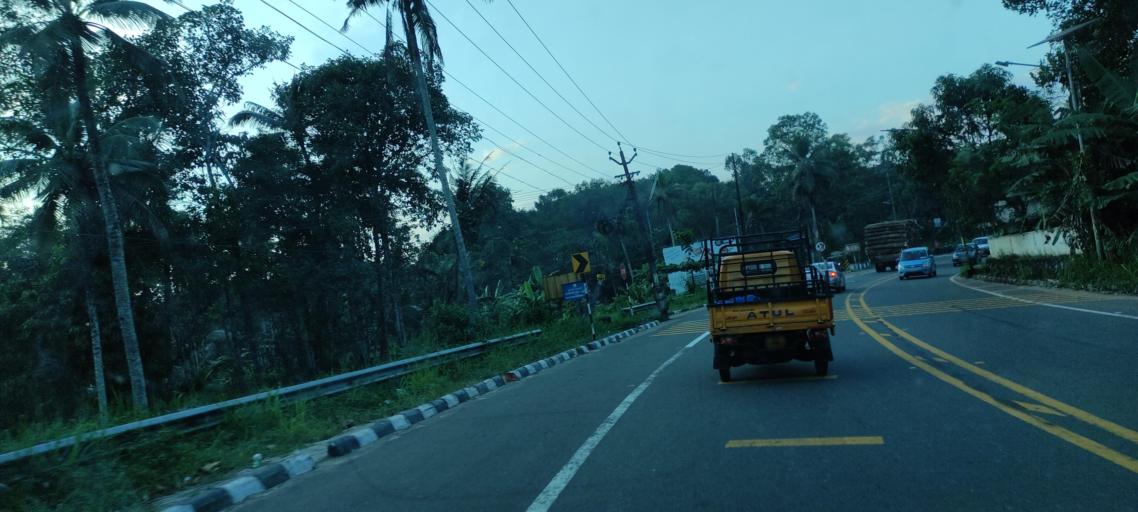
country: IN
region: Kerala
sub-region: Pattanamtitta
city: Adur
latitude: 9.1520
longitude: 76.7277
